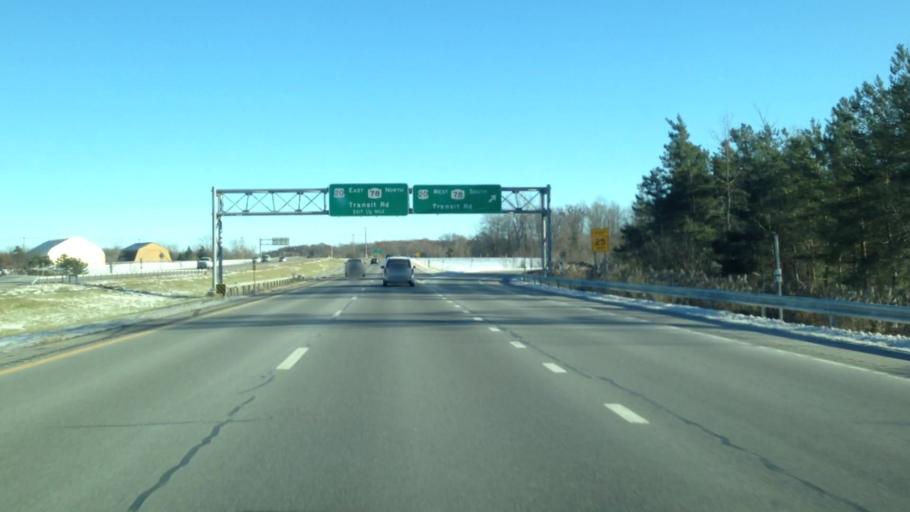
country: US
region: New York
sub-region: Erie County
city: Elma Center
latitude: 42.8364
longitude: -78.7026
